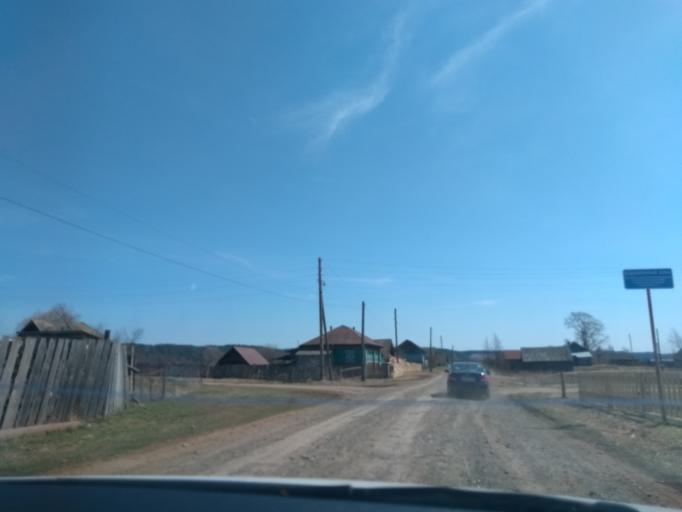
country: RU
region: Perm
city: Uinskoye
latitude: 57.1781
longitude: 56.5709
